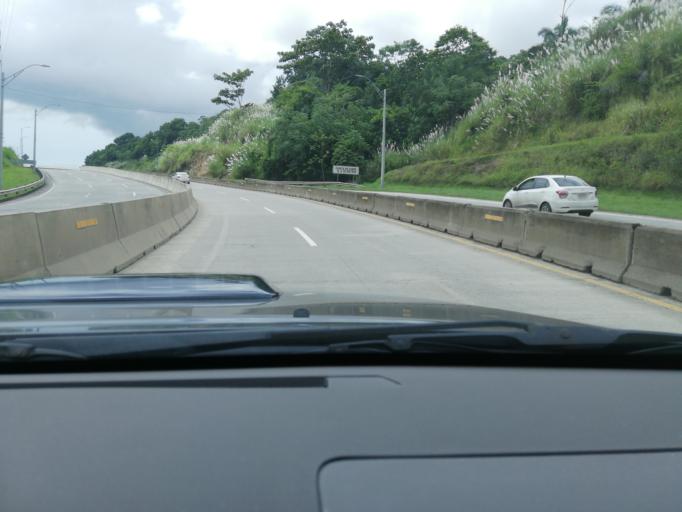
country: PA
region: Panama
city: San Miguelito
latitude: 9.0795
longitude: -79.4625
